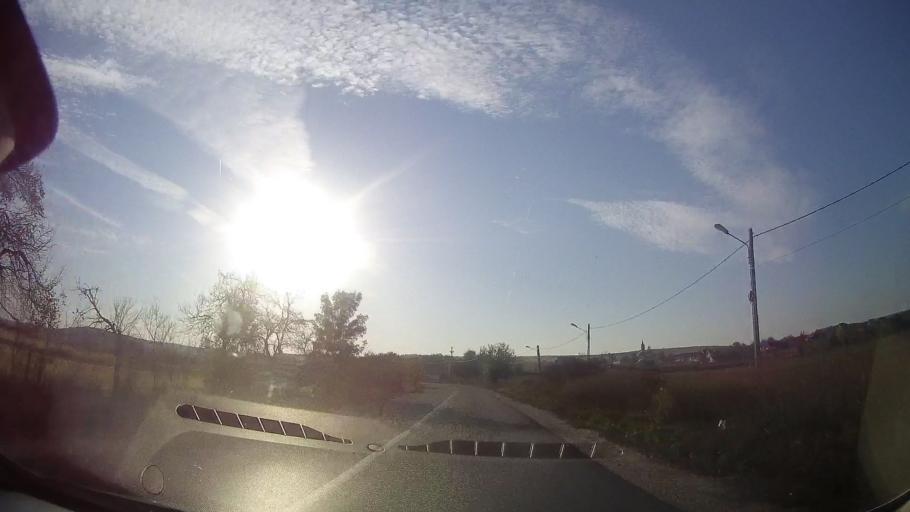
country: RO
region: Timis
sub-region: Comuna Masloc
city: Masloc
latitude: 45.9704
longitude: 21.4745
